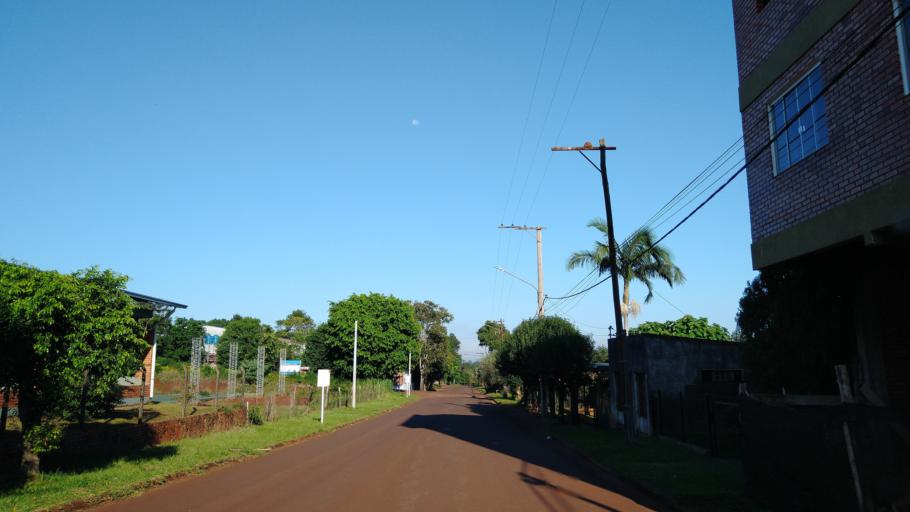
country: AR
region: Misiones
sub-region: Departamento de Montecarlo
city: Montecarlo
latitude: -26.5650
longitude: -54.7634
